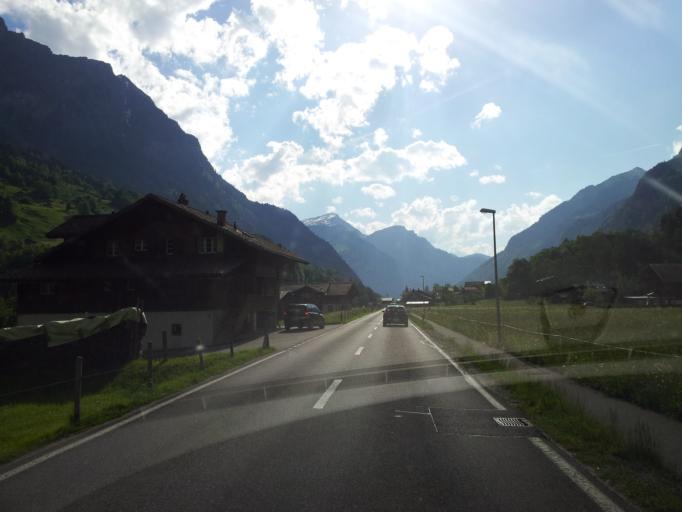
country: CH
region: Bern
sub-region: Interlaken-Oberhasli District
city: Grindelwald
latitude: 46.6364
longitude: 7.9838
